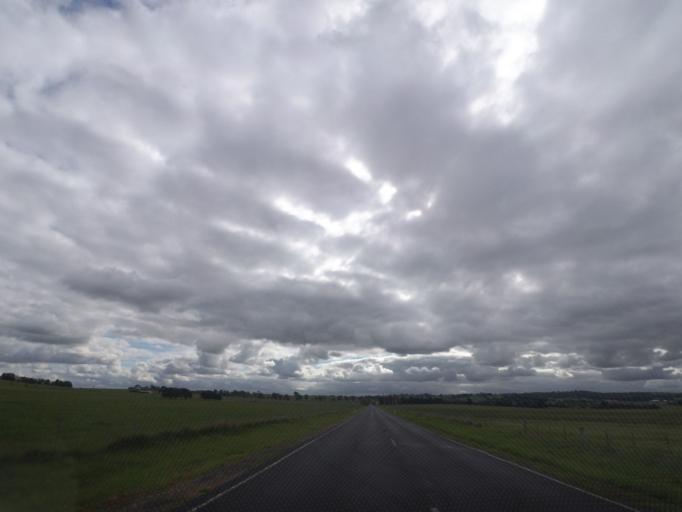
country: AU
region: Victoria
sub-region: Whittlesea
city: Whittlesea
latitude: -37.5264
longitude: 145.0906
